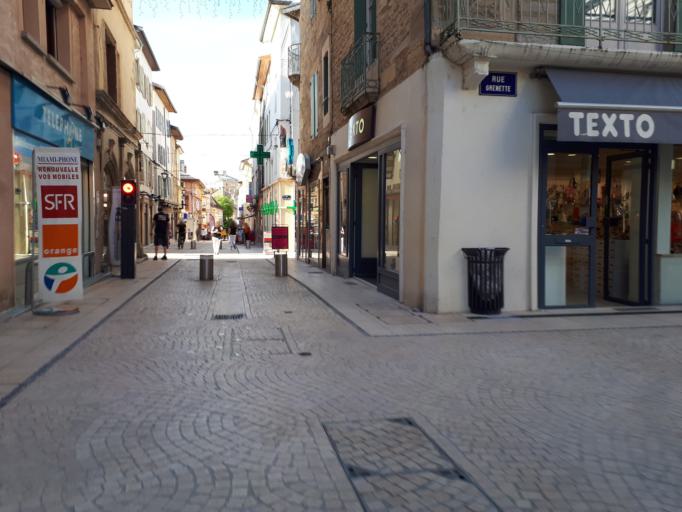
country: FR
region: Rhone-Alpes
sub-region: Departement de l'Isere
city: Bourgoin-Jallieu
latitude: 45.5864
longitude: 5.2777
